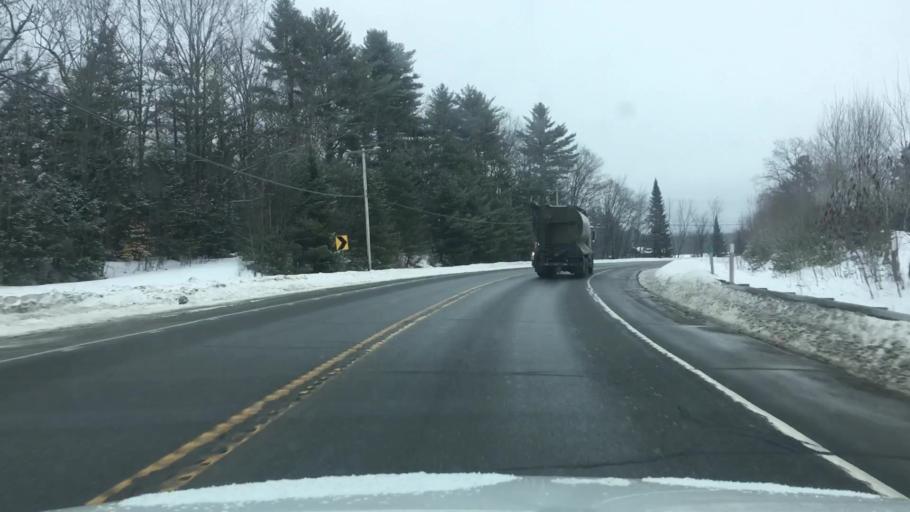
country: US
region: Maine
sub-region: Franklin County
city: New Sharon
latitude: 44.6361
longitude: -70.0508
